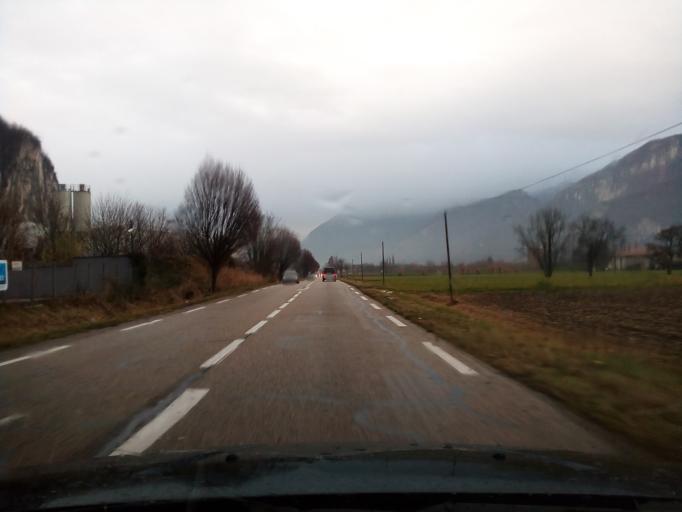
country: FR
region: Rhone-Alpes
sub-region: Departement de l'Isere
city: La Buisse
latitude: 45.3148
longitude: 5.6222
